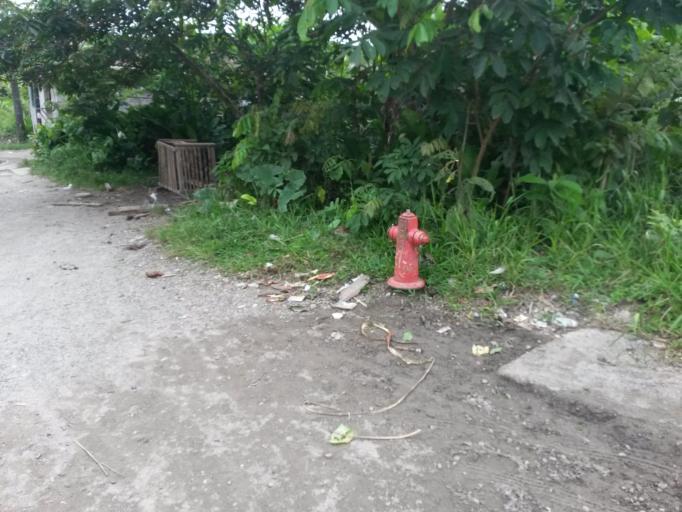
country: CO
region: Cauca
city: Guapi
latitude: 2.5704
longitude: -77.8905
